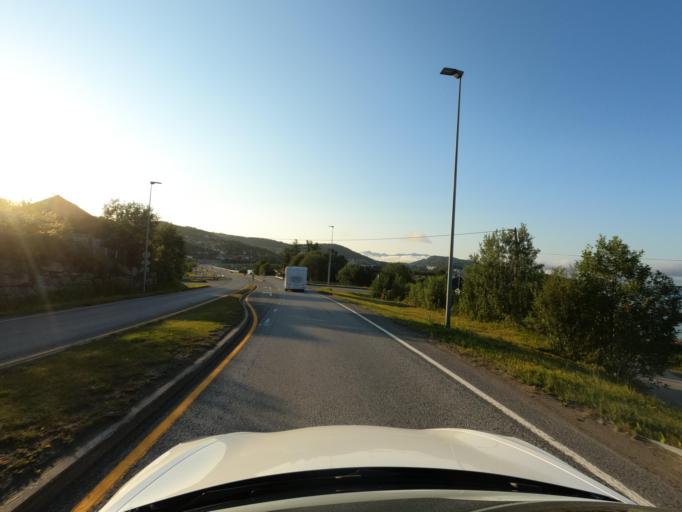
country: NO
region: Troms
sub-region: Harstad
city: Harstad
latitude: 68.7595
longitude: 16.5672
